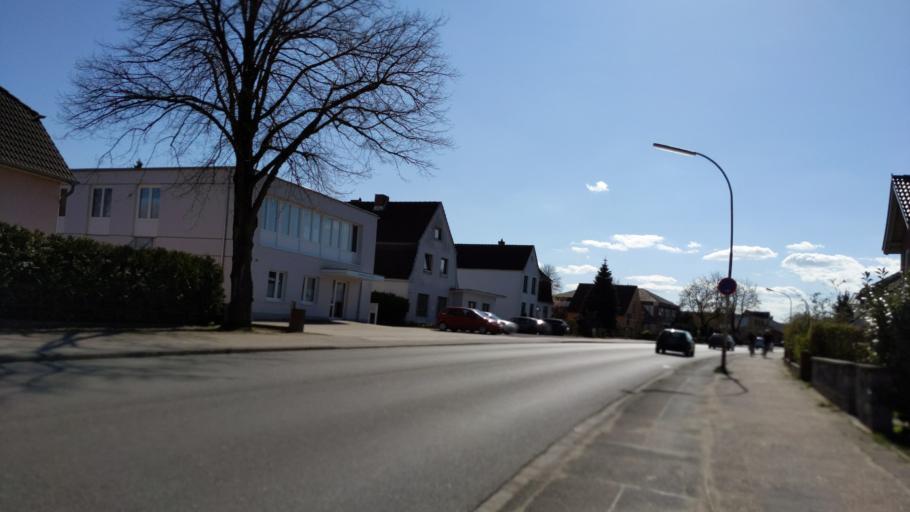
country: DE
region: Schleswig-Holstein
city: Eutin
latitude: 54.1313
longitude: 10.5923
